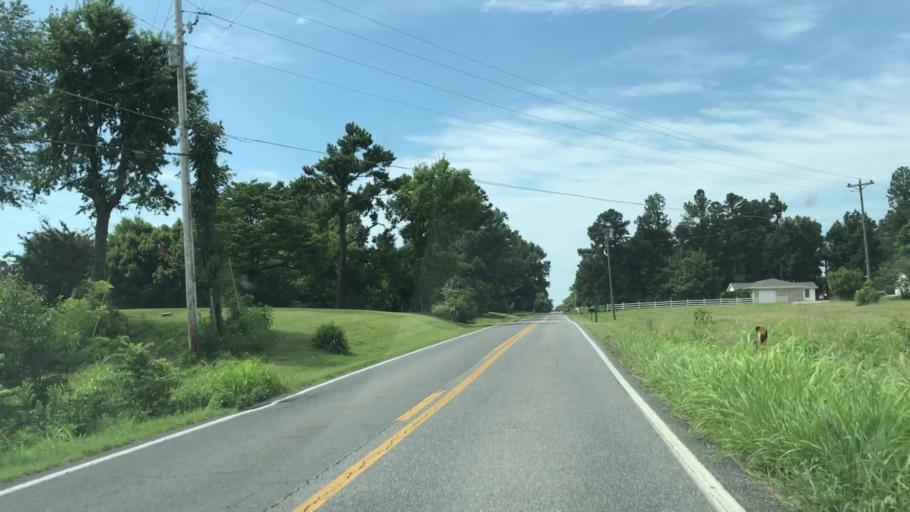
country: US
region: Kentucky
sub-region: Graves County
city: Mayfield
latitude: 36.7826
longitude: -88.5958
